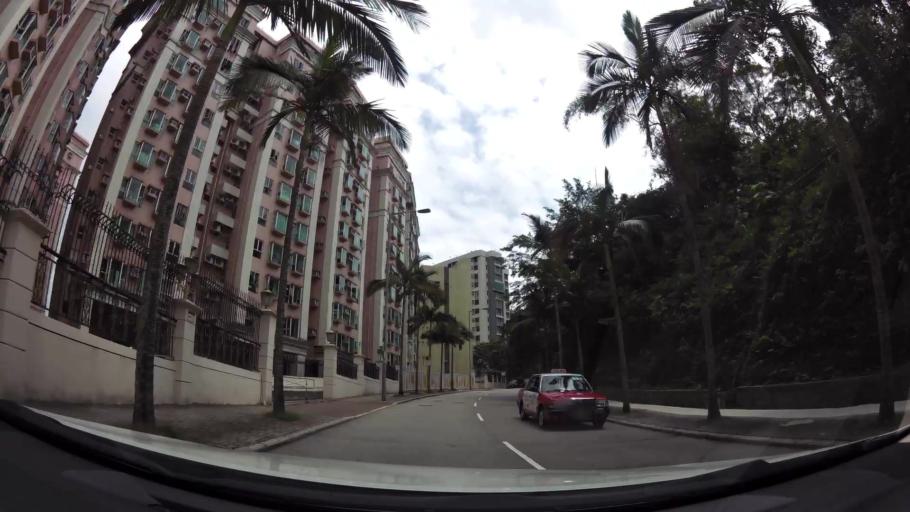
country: HK
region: Wanchai
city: Wan Chai
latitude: 22.2874
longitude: 114.2037
